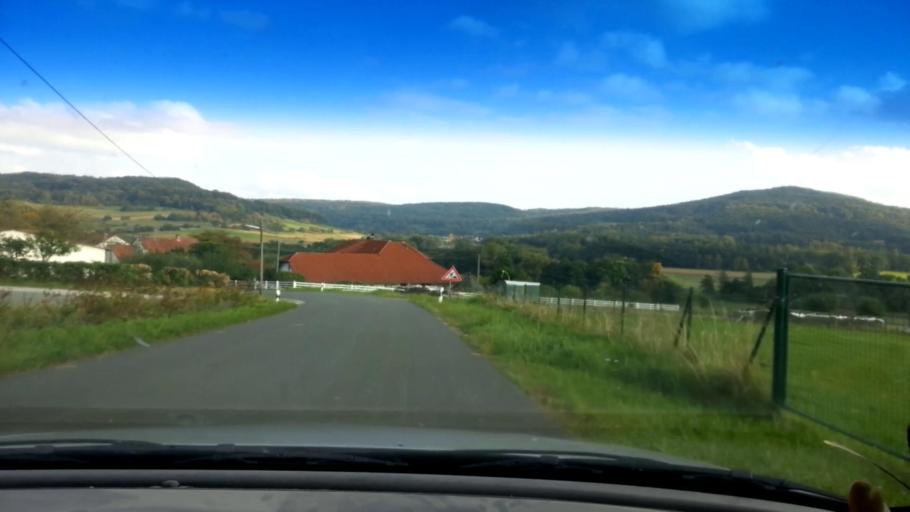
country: DE
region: Bavaria
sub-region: Upper Franconia
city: Schesslitz
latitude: 50.0070
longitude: 11.0585
